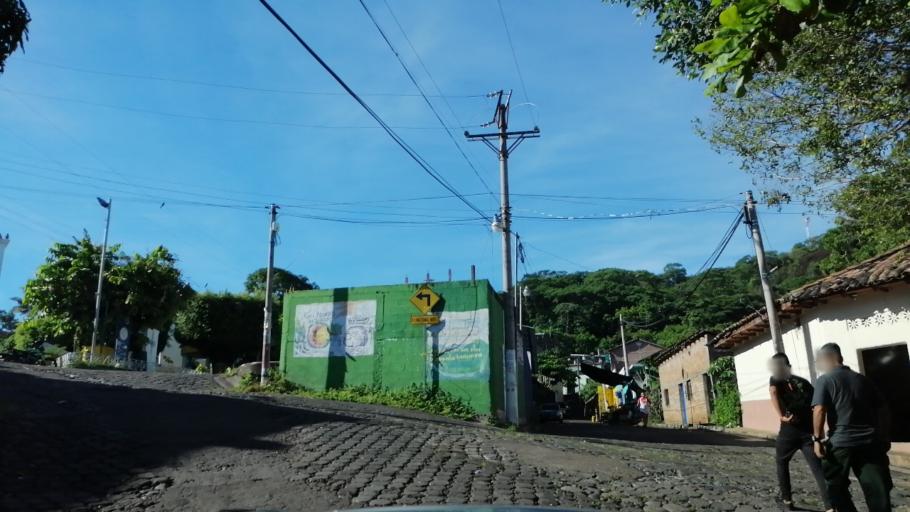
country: SV
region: Morazan
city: Cacaopera
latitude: 13.7738
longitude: -88.0798
